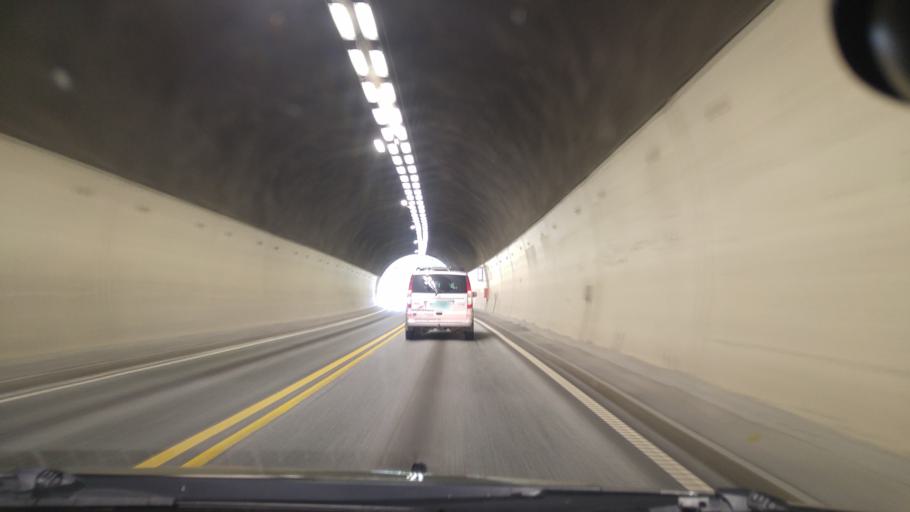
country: NO
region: Sor-Trondelag
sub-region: Malvik
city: Hommelvik
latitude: 63.4035
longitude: 10.8007
